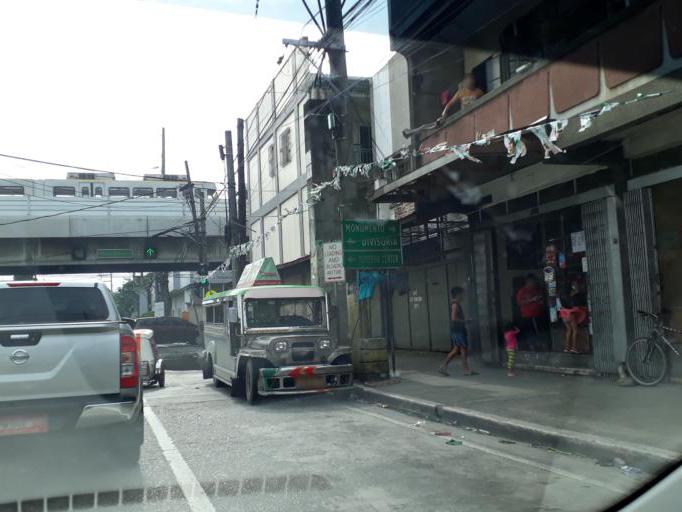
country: PH
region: Metro Manila
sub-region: City of Manila
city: Manila
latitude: 14.6280
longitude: 120.9835
